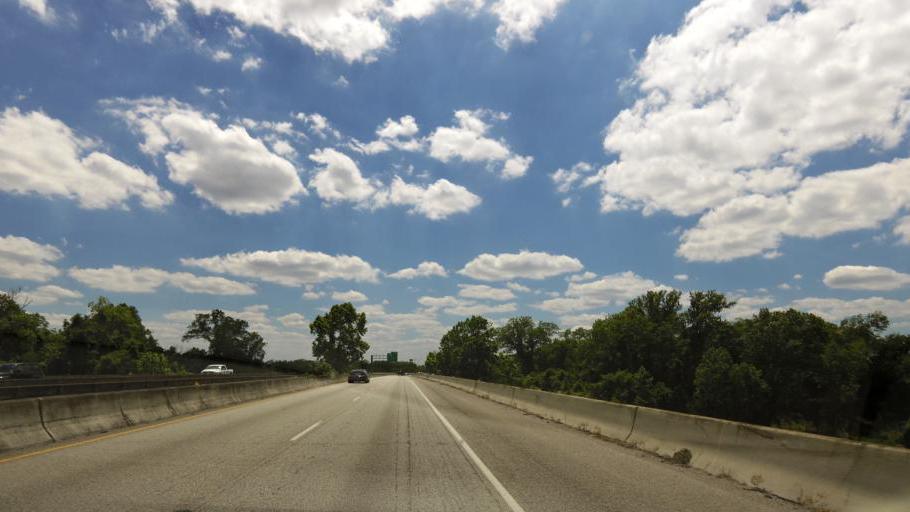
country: US
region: Texas
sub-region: Colorado County
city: Columbus
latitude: 29.6965
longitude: -96.5321
